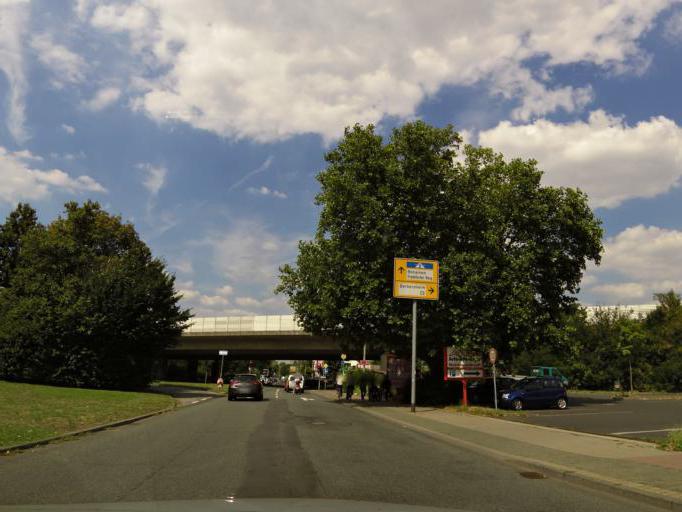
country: DE
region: Hesse
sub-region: Regierungsbezirk Darmstadt
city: Frankfurt am Main
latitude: 50.1586
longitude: 8.6887
